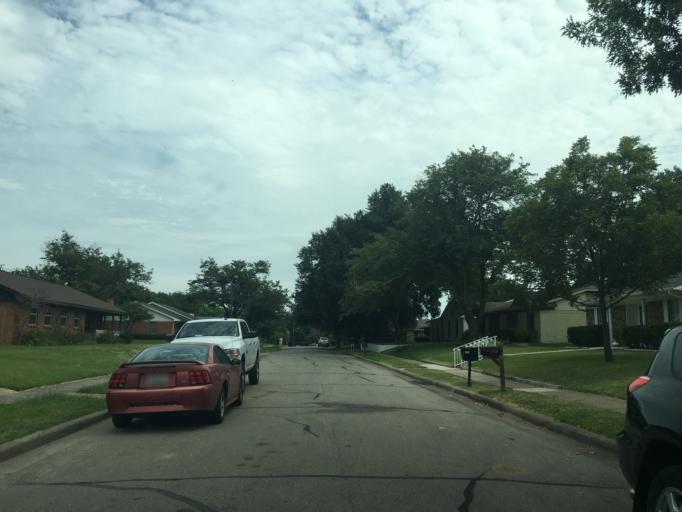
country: US
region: Texas
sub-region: Collin County
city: Wylie
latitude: 33.0074
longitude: -96.5329
